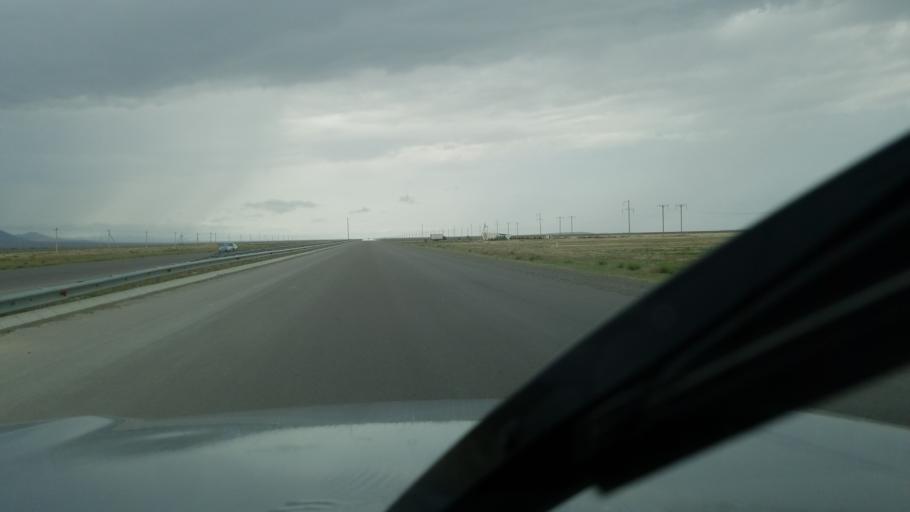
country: TM
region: Balkan
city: Serdar
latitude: 39.0431
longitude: 56.1488
